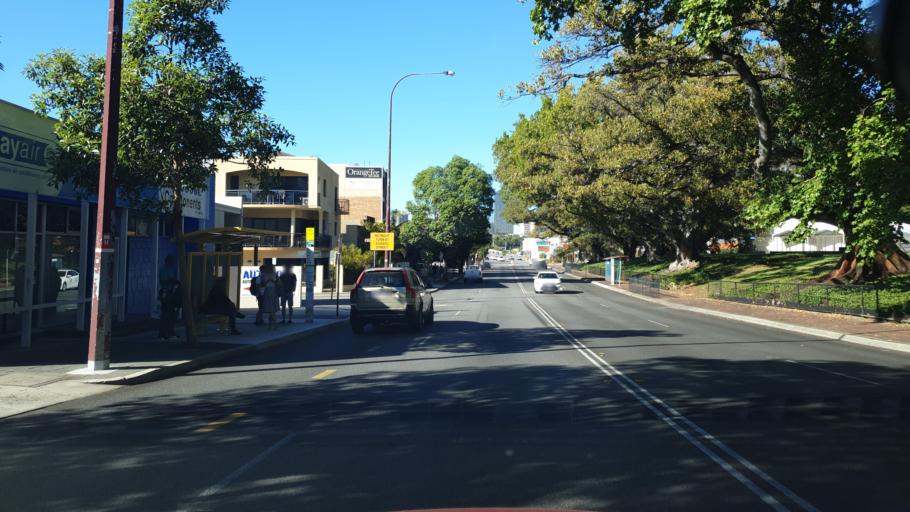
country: AU
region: Western Australia
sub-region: Vincent
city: Mount Lawley
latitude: -31.9460
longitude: 115.8719
